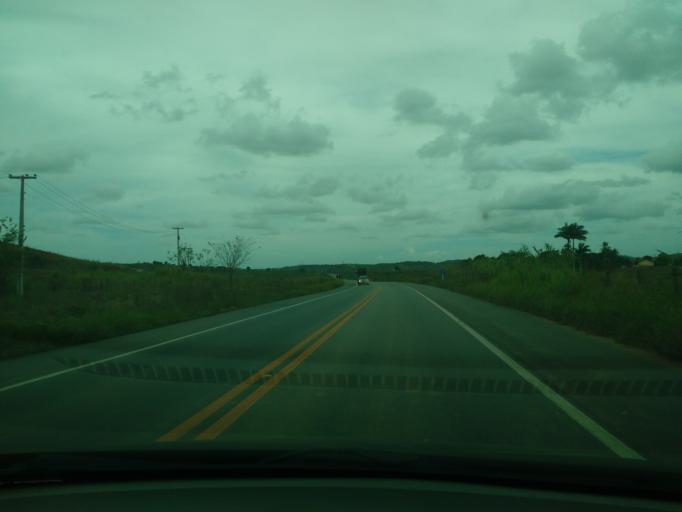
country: BR
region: Alagoas
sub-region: Murici
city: Murici
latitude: -9.2895
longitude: -35.9614
